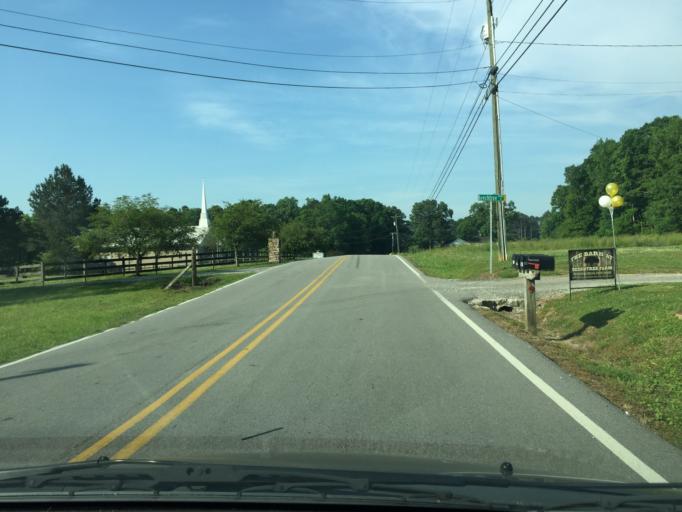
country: US
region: Tennessee
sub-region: Hamilton County
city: Collegedale
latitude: 35.0636
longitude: -85.0115
